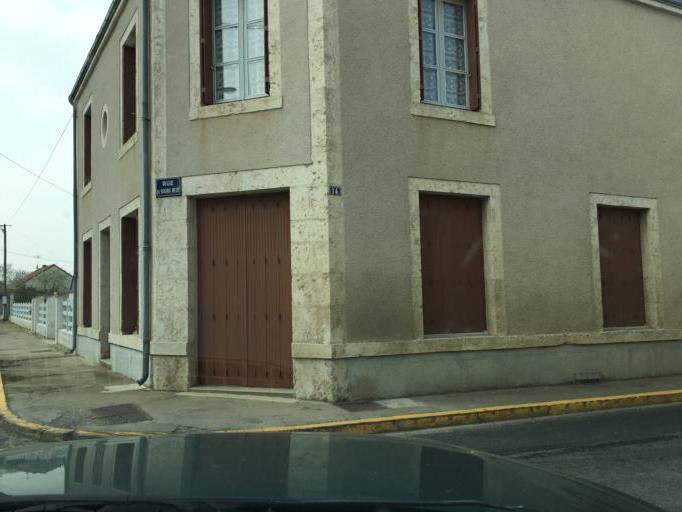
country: FR
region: Centre
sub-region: Departement du Loiret
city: Beaugency
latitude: 47.8295
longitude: 1.5714
